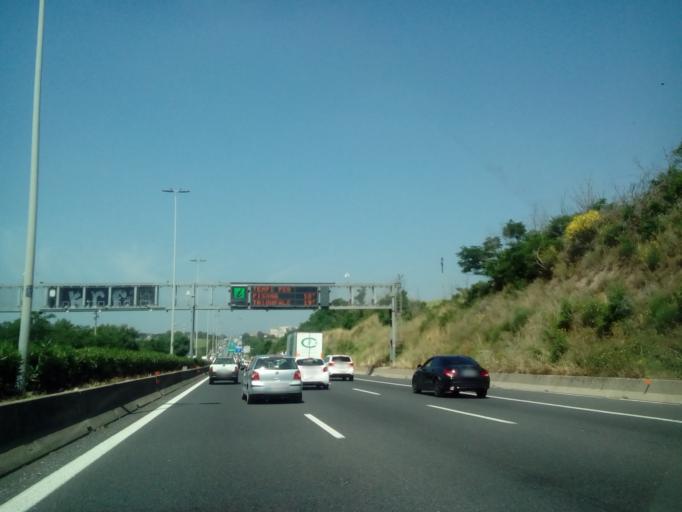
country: IT
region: Latium
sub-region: Citta metropolitana di Roma Capitale
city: Selcetta
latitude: 41.7988
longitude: 12.4713
